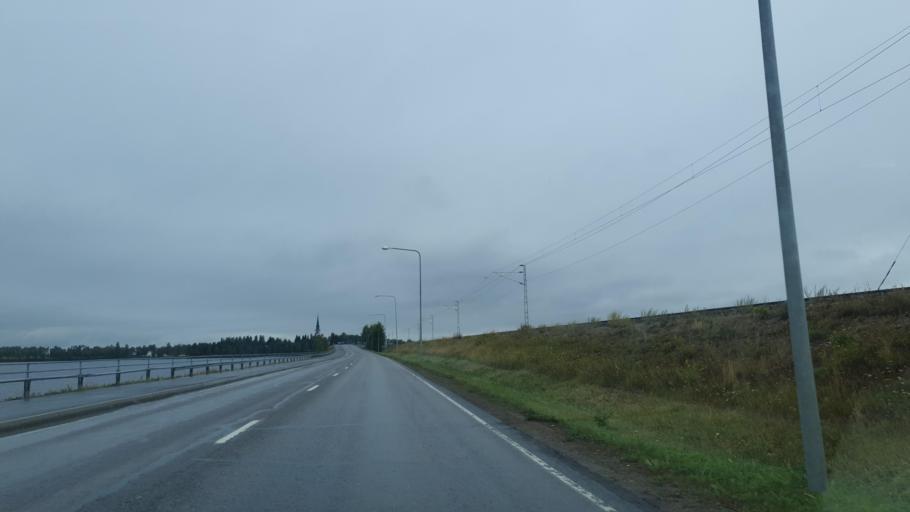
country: FI
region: Lapland
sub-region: Itae-Lappi
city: Kemijaervi
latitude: 66.7159
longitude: 27.4620
